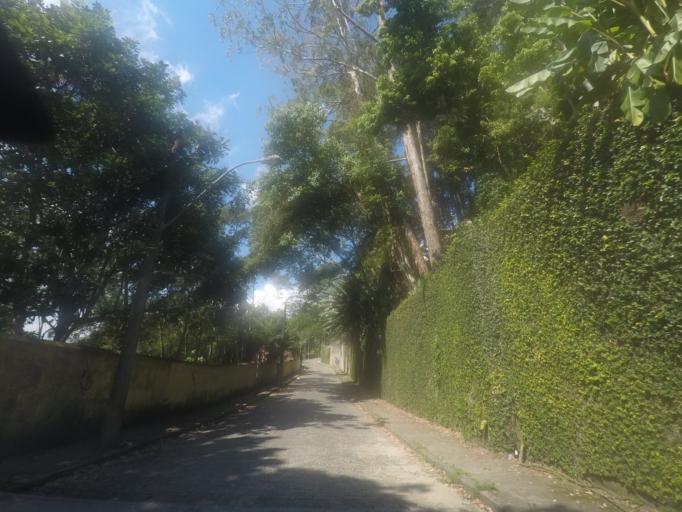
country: BR
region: Rio de Janeiro
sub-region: Petropolis
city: Petropolis
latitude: -22.5098
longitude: -43.1804
